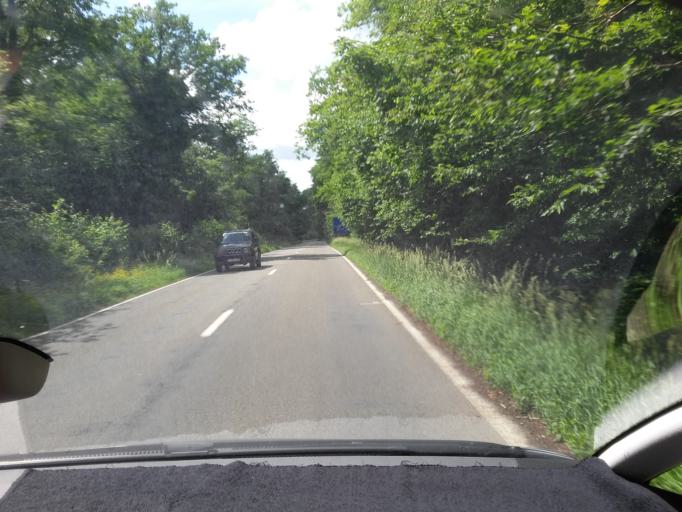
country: BE
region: Wallonia
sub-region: Province de Namur
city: Rochefort
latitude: 50.1236
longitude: 5.2575
